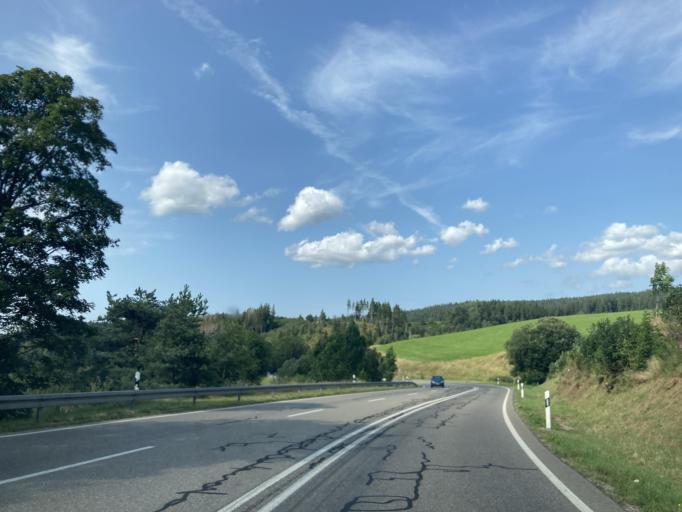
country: DE
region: Baden-Wuerttemberg
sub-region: Freiburg Region
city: Sankt Georgen im Schwarzwald
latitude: 48.1272
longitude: 8.2897
